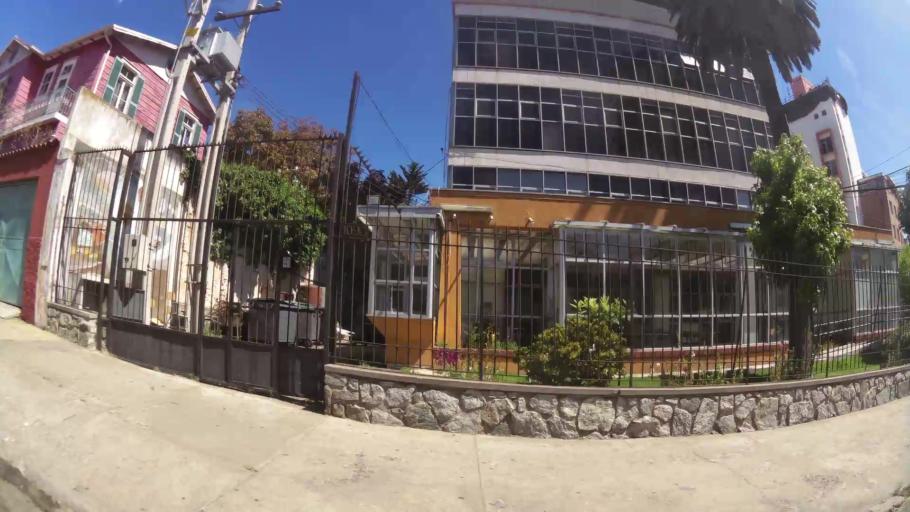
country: CL
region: Valparaiso
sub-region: Provincia de Valparaiso
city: Valparaiso
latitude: -33.0267
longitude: -71.6382
